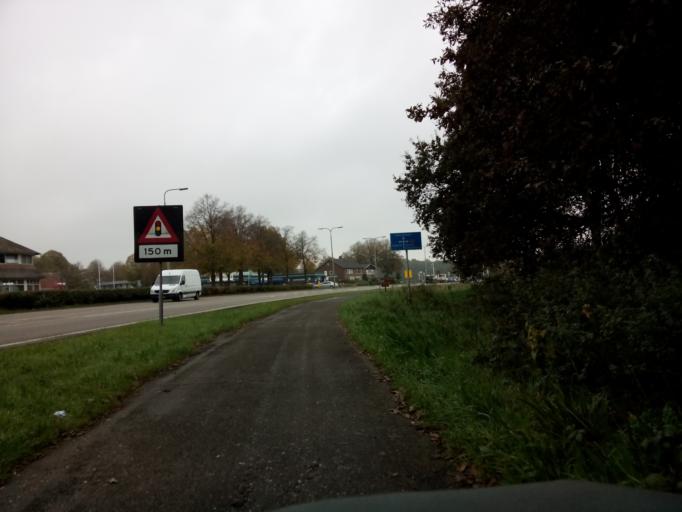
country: NL
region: Utrecht
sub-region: Gemeente Leusden
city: Leusden
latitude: 52.1720
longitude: 5.4364
